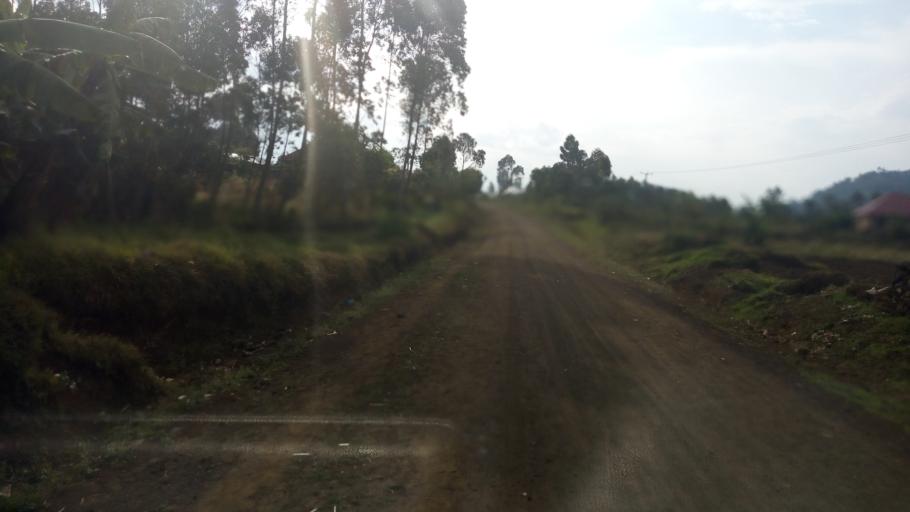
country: UG
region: Western Region
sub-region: Kisoro District
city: Kisoro
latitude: -1.3118
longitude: 29.7194
